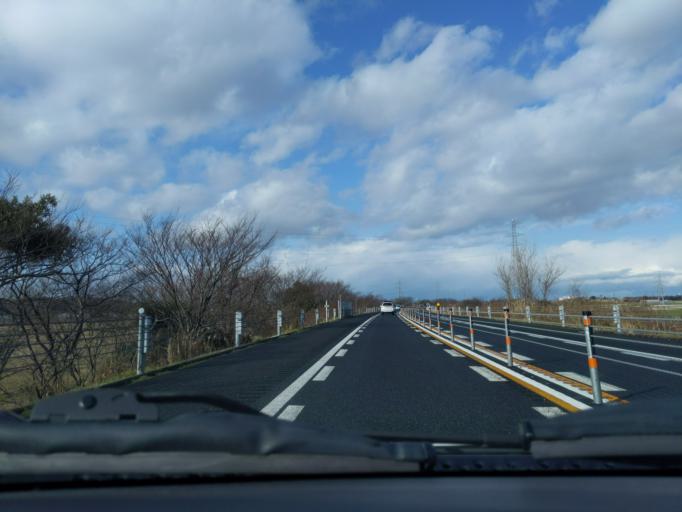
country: JP
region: Niigata
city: Niitsu-honcho
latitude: 37.7838
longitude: 139.1667
